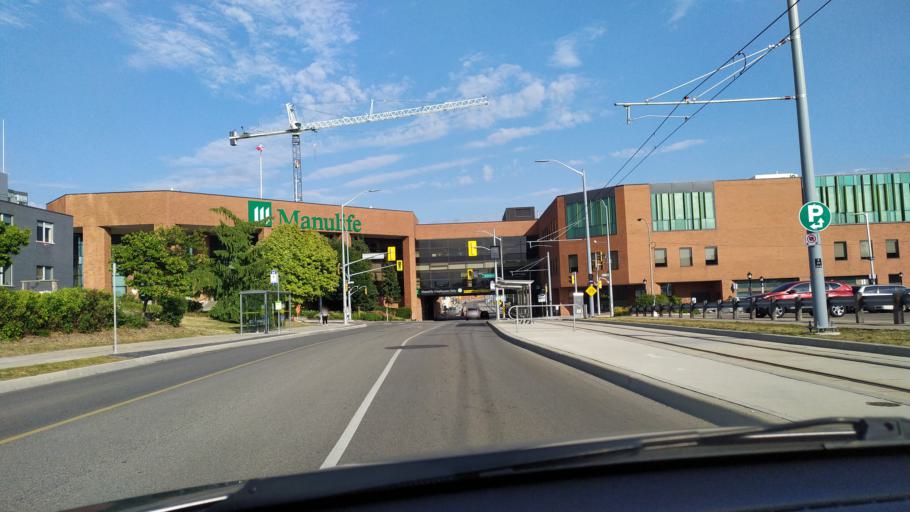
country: CA
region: Ontario
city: Waterloo
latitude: 43.4510
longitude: -80.4959
